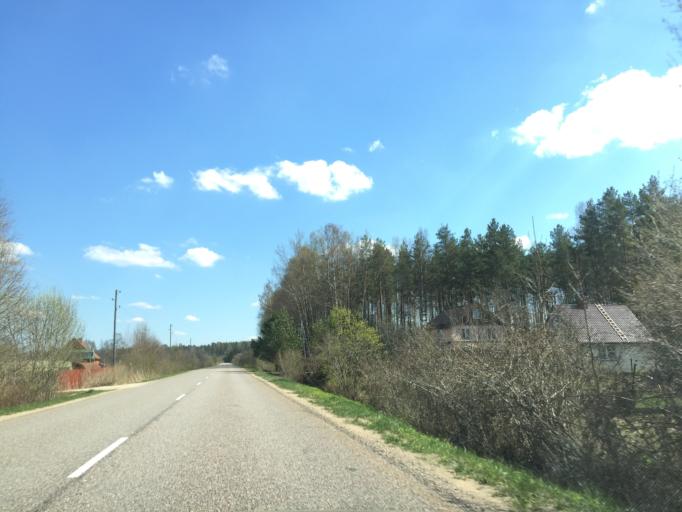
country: LV
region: Saulkrastu
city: Saulkrasti
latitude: 57.2400
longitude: 24.4430
